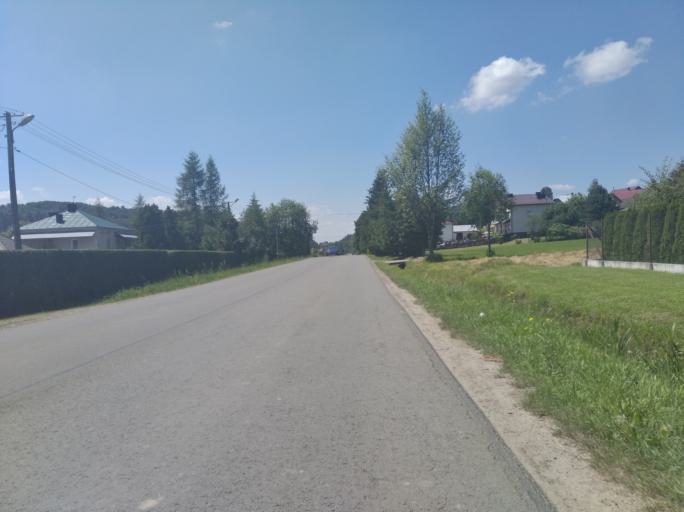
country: PL
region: Subcarpathian Voivodeship
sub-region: Powiat brzozowski
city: Niebocko
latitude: 49.6755
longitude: 22.0982
